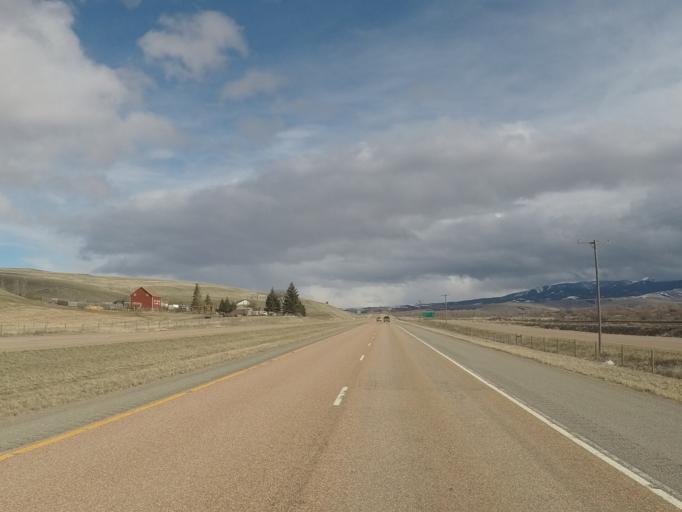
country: US
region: Montana
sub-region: Granite County
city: Philipsburg
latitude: 46.6560
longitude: -113.1284
